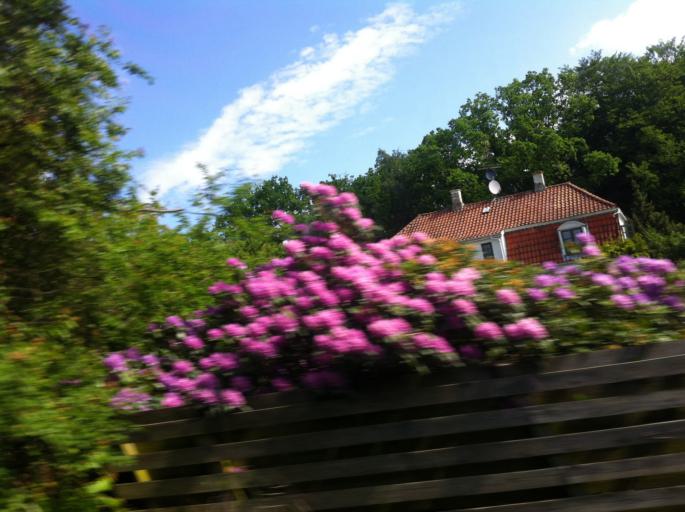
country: DK
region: Capital Region
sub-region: Helsingor Kommune
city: Hornbaek
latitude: 56.0934
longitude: 12.4201
